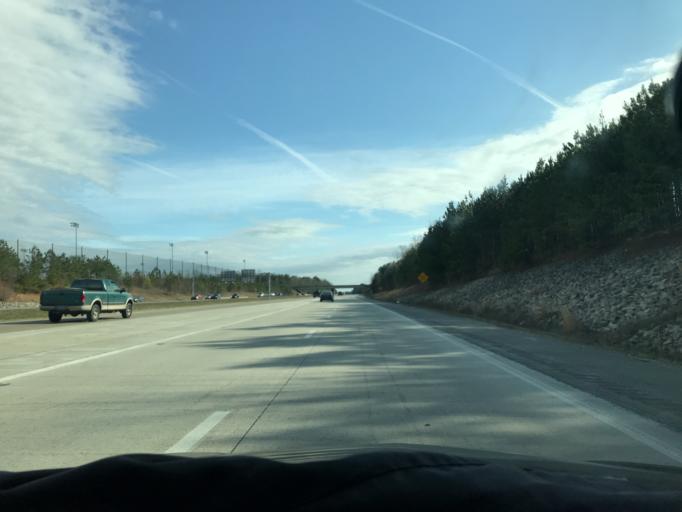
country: US
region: Virginia
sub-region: Chesterfield County
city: Brandermill
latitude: 37.4550
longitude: -77.6380
